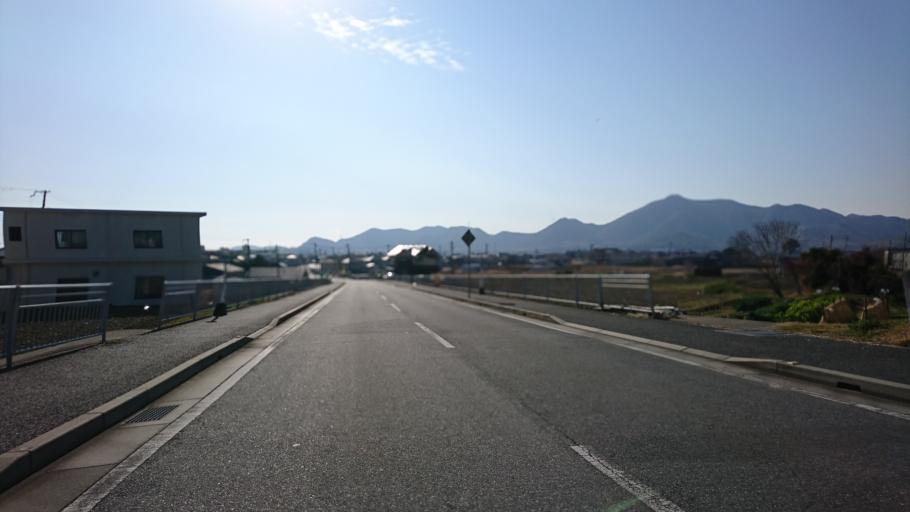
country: JP
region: Hyogo
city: Kakogawacho-honmachi
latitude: 34.8239
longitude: 134.8254
